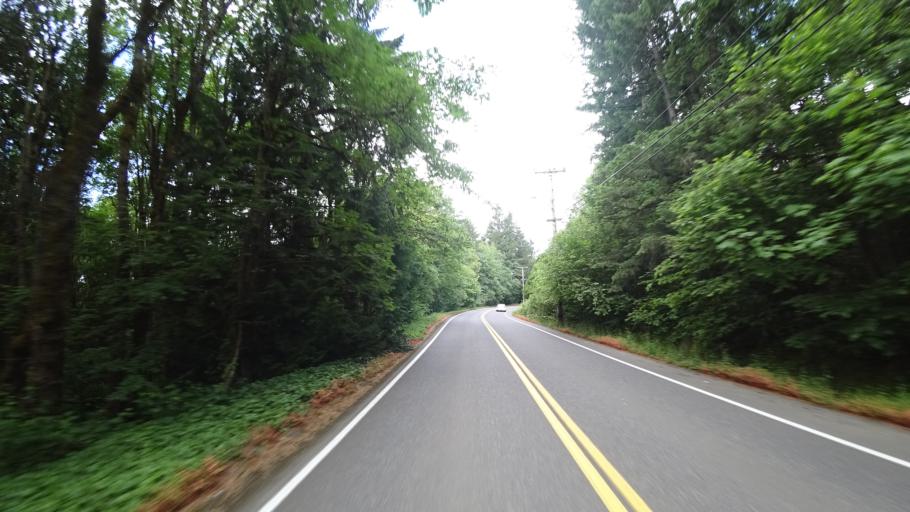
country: US
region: Oregon
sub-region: Clackamas County
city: Lake Oswego
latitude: 45.4473
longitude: -122.6767
